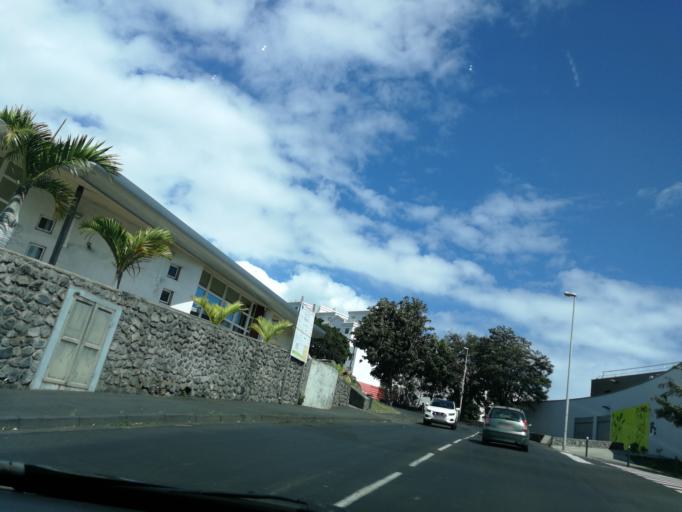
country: RE
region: Reunion
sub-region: Reunion
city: Saint-Denis
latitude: -20.9057
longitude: 55.4834
